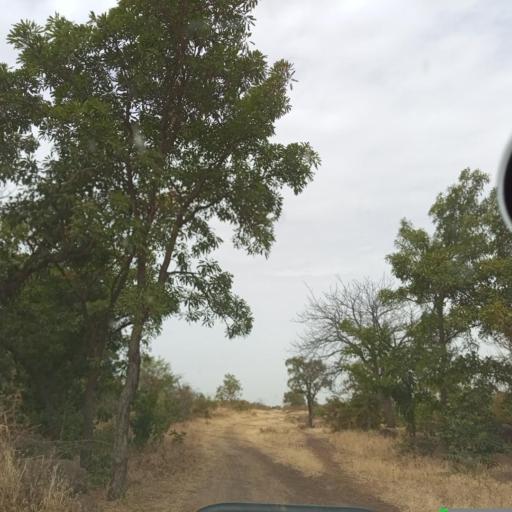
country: ML
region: Koulikoro
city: Kolokani
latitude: 13.2088
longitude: -7.8427
